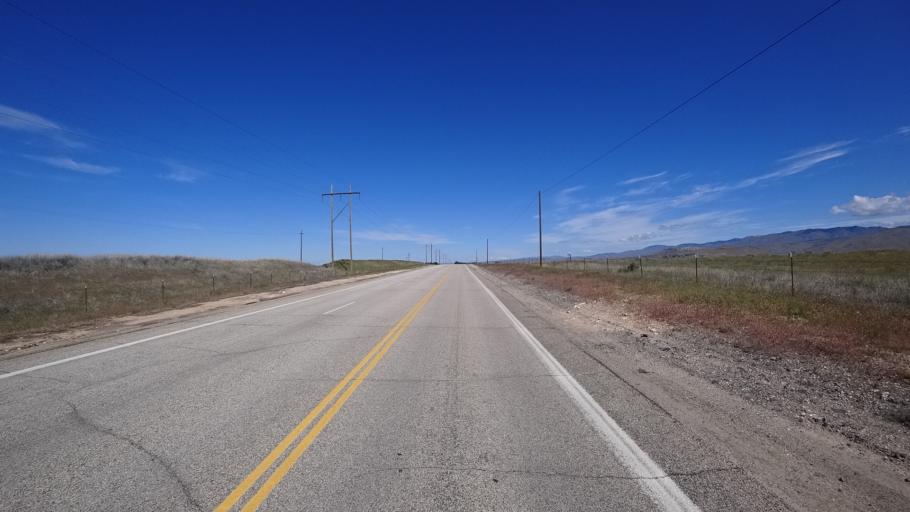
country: US
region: Idaho
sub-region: Ada County
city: Boise
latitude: 43.5356
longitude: -116.1438
